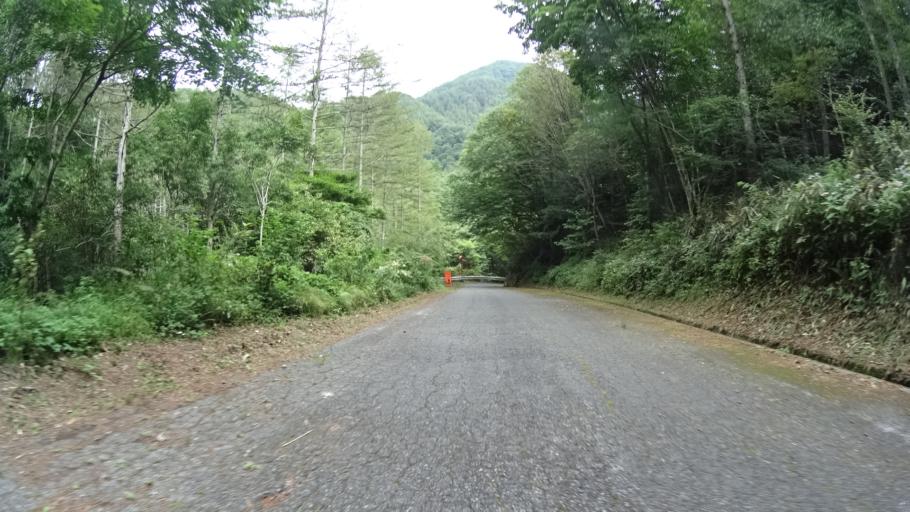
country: JP
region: Yamanashi
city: Nirasaki
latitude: 35.8042
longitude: 138.5267
